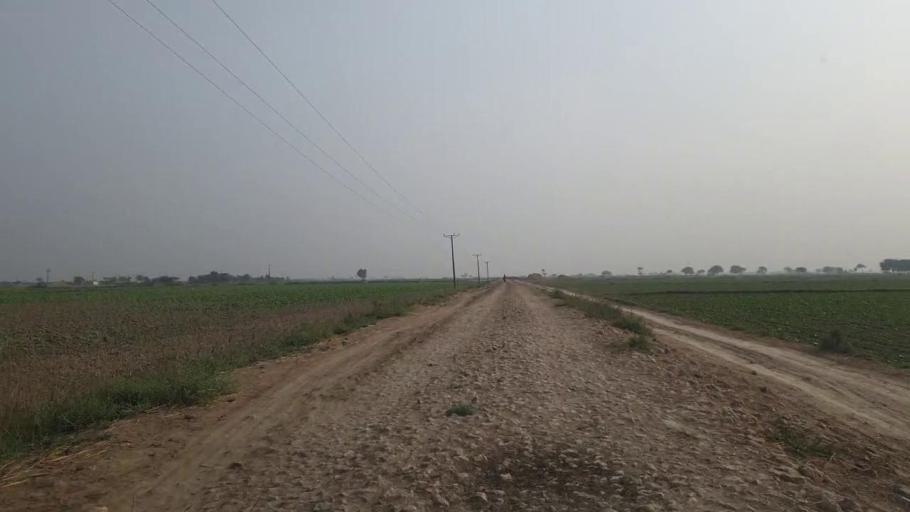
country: PK
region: Sindh
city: Mirpur Batoro
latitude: 24.5616
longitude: 68.4186
